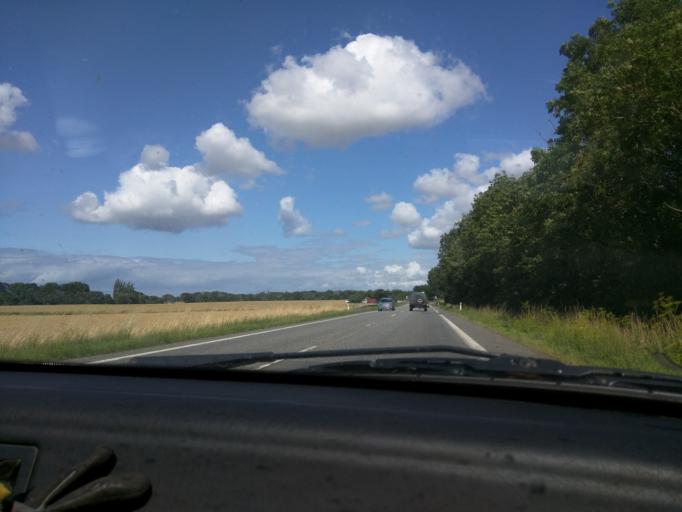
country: DK
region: Zealand
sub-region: Kalundborg Kommune
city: Svebolle
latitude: 55.6668
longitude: 11.2781
